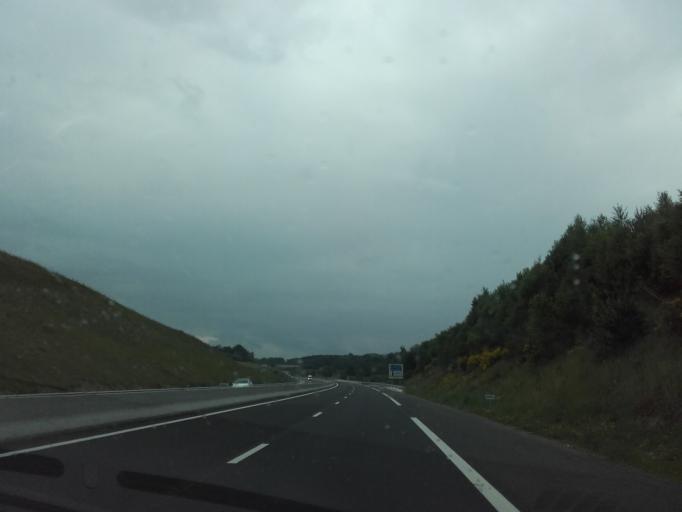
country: FR
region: Limousin
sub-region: Departement de la Correze
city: Saint-Mexant
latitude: 45.2943
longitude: 1.5954
